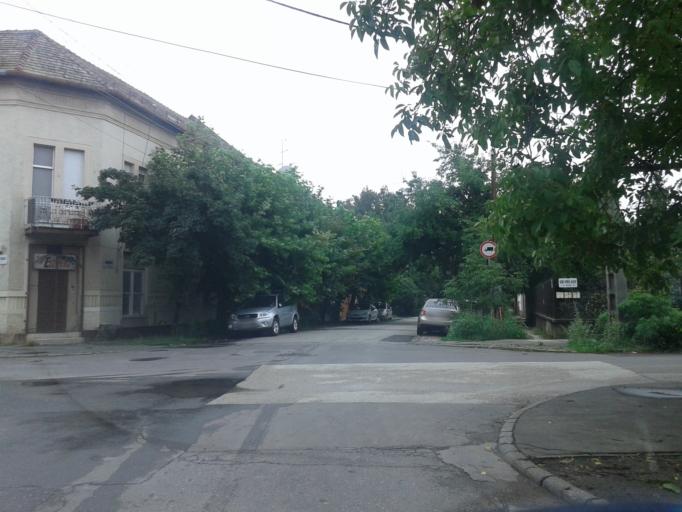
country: HU
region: Csongrad
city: Szeged
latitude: 46.2516
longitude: 20.1614
